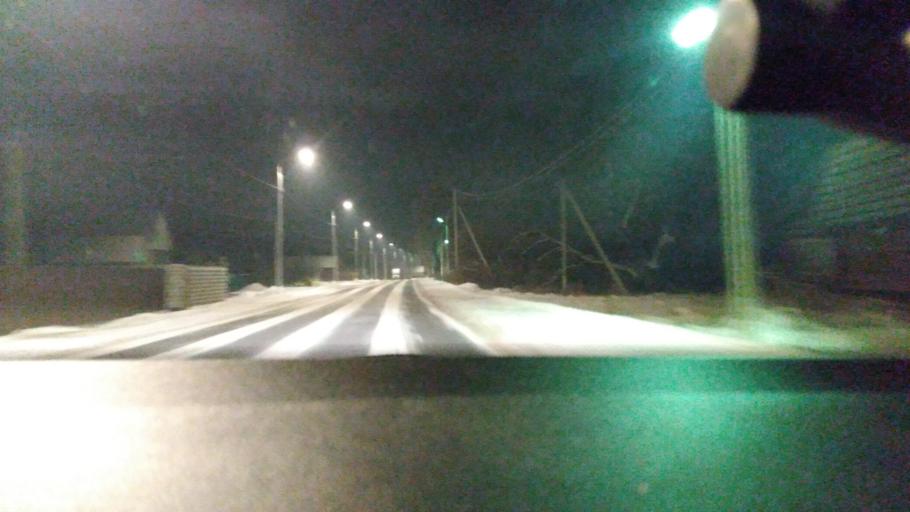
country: RU
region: Moskovskaya
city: Krasnaya Poyma
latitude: 55.1021
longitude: 38.9940
